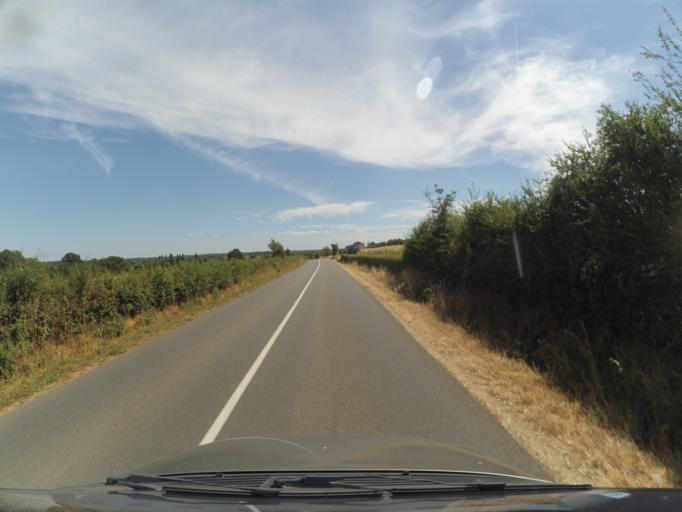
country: FR
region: Poitou-Charentes
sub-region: Departement de la Vienne
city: Availles-Limouzine
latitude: 46.1201
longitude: 0.5625
